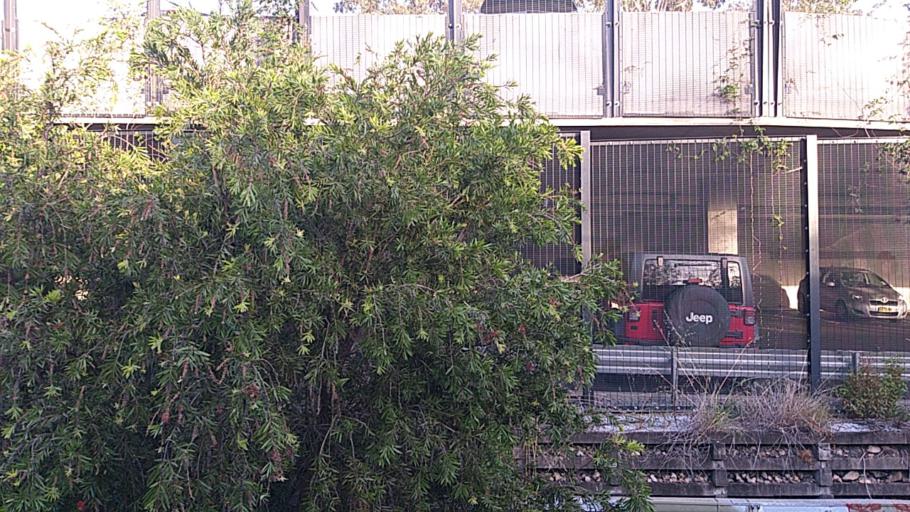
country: AU
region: New South Wales
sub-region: Hurstville
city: Oatley
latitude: -33.9812
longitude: 151.0789
